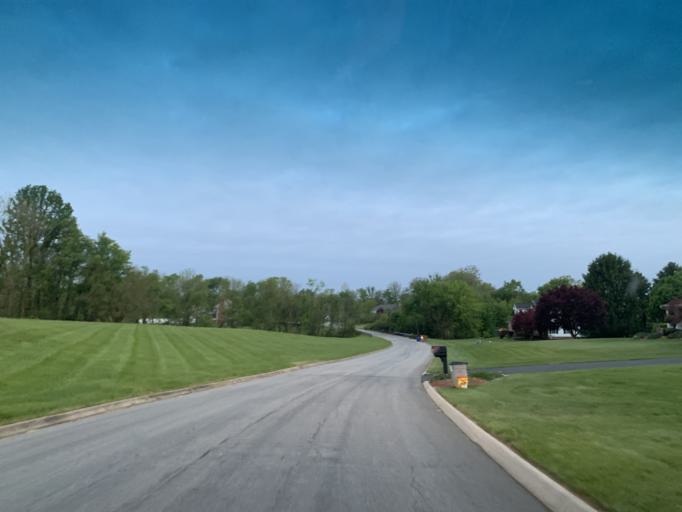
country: US
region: Maryland
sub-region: Harford County
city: South Bel Air
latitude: 39.5898
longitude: -76.2691
